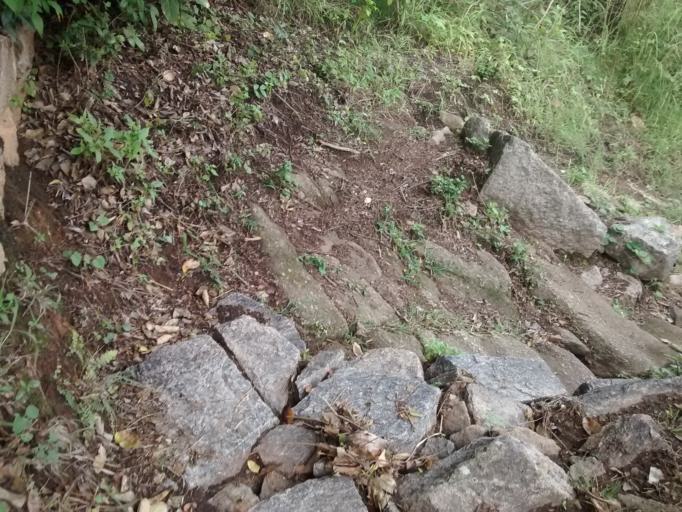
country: IN
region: Karnataka
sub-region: Tumkur
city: Tumkur
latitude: 13.3778
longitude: 77.2083
